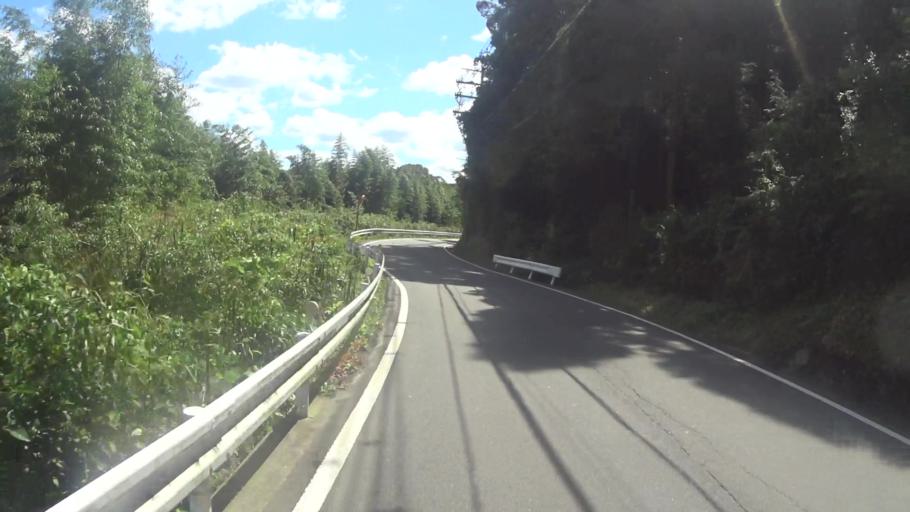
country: JP
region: Nara
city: Nara-shi
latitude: 34.7553
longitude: 135.8551
